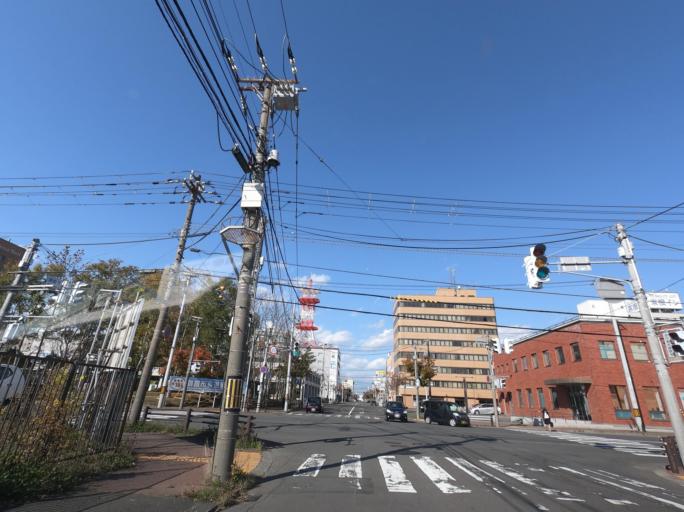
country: JP
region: Hokkaido
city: Kushiro
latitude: 42.9841
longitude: 144.3828
